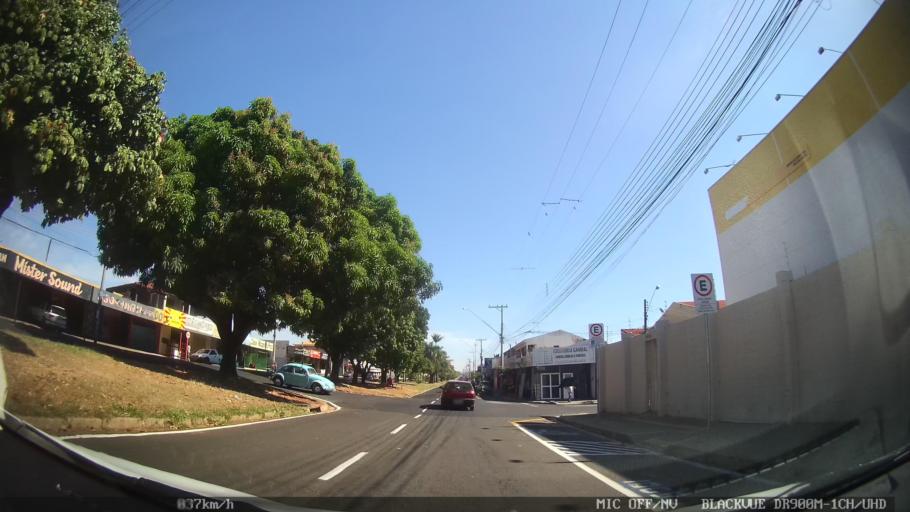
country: BR
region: Sao Paulo
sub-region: Sao Jose Do Rio Preto
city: Sao Jose do Rio Preto
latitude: -20.7764
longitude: -49.4079
